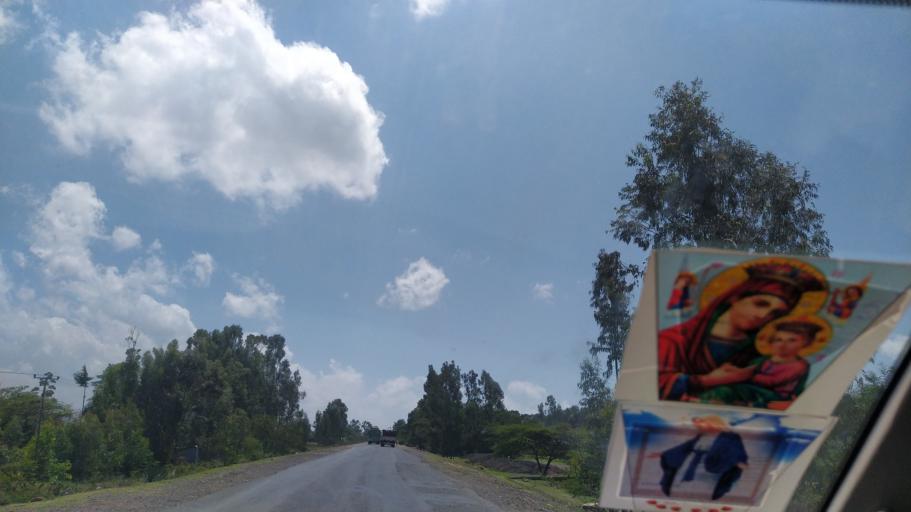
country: ET
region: Southern Nations, Nationalities, and People's Region
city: Butajira
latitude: 7.7603
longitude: 38.1329
